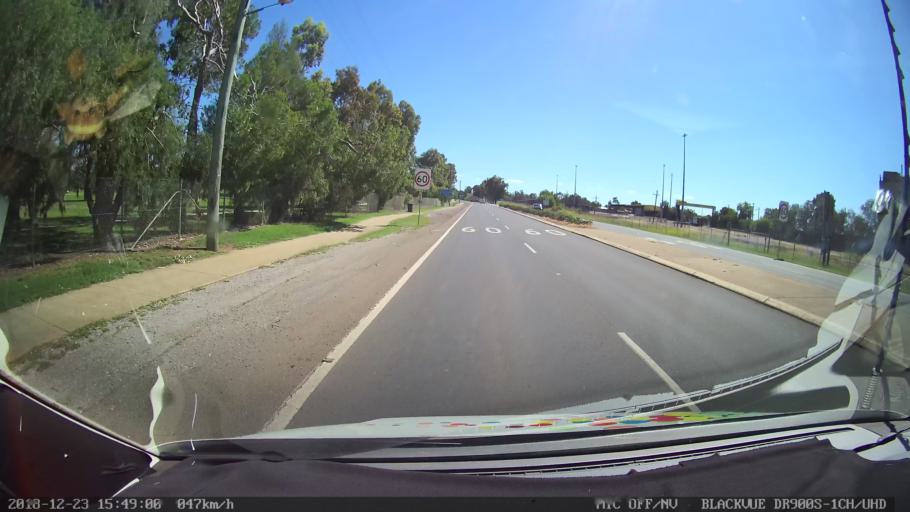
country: AU
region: New South Wales
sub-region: Tamworth Municipality
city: South Tamworth
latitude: -31.0964
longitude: 150.9098
